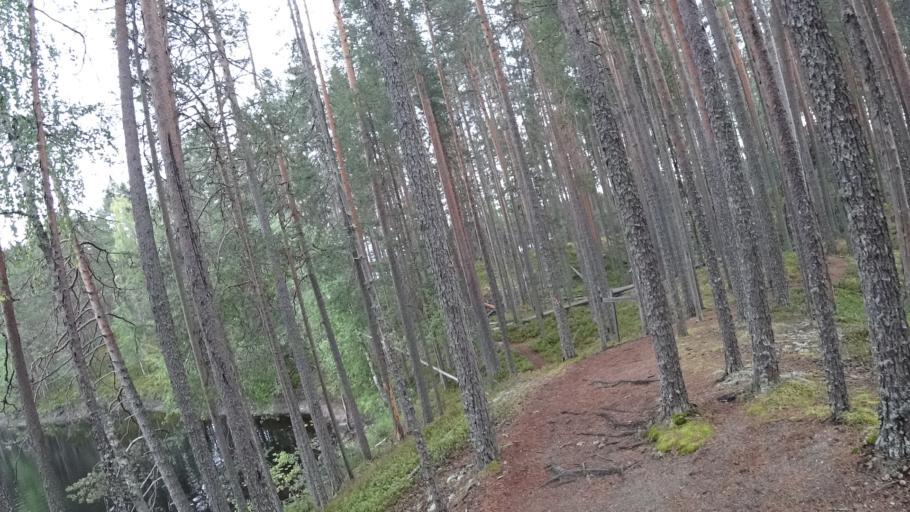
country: FI
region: North Karelia
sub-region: Joensuu
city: Ilomantsi
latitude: 62.5793
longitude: 31.1669
